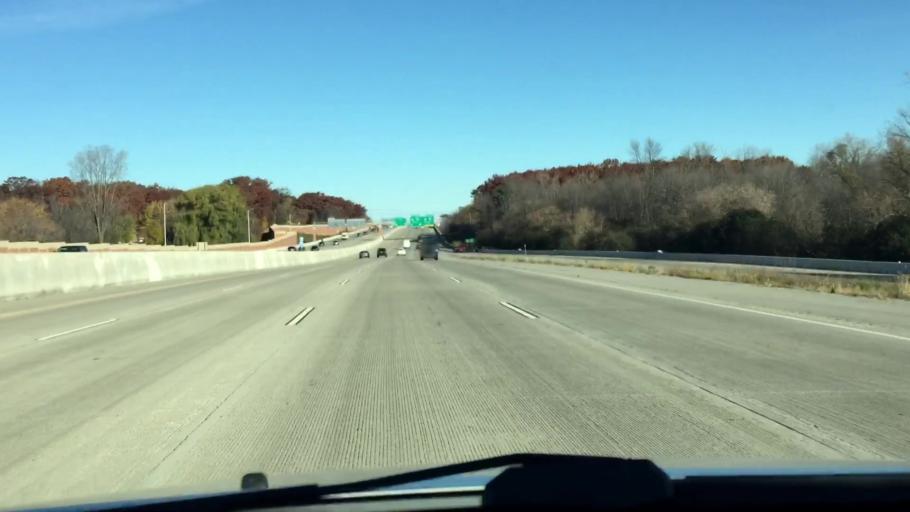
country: US
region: Wisconsin
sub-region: Brown County
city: Ashwaubenon
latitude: 44.5113
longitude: -88.0825
